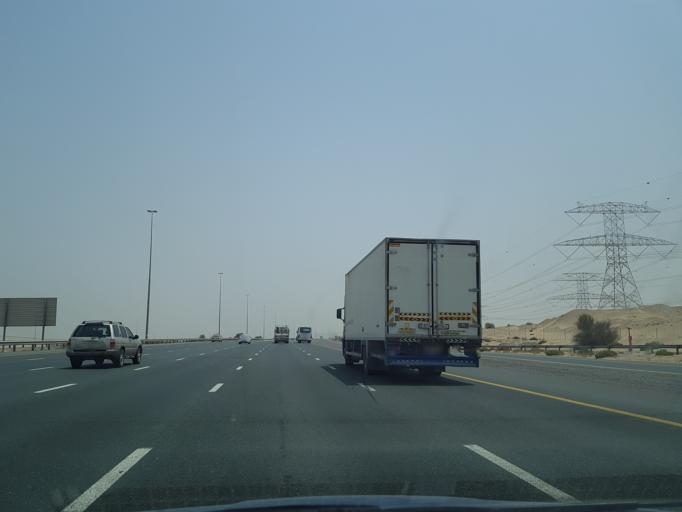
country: AE
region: Dubai
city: Dubai
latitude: 25.0580
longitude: 55.3198
